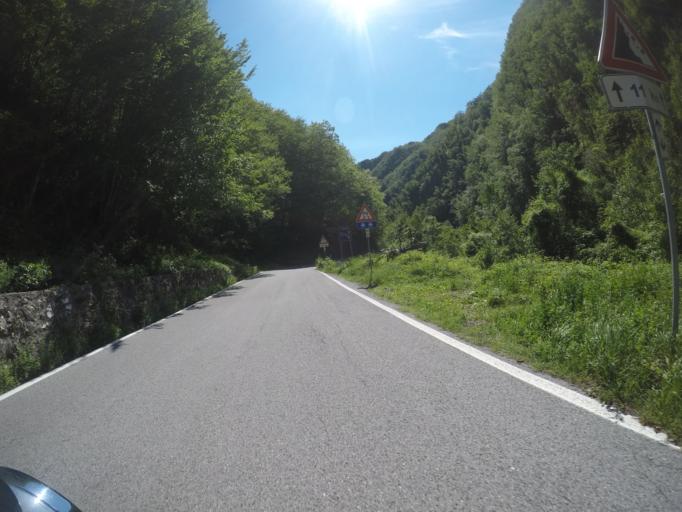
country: IT
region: Tuscany
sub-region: Provincia di Lucca
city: Fontana delle Monache
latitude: 44.0610
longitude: 10.2999
